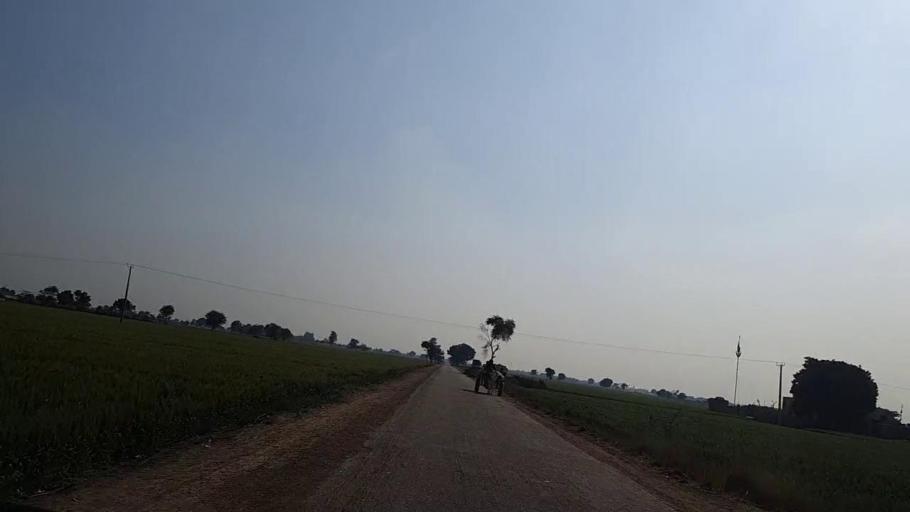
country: PK
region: Sindh
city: Sakrand
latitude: 26.0945
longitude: 68.2904
